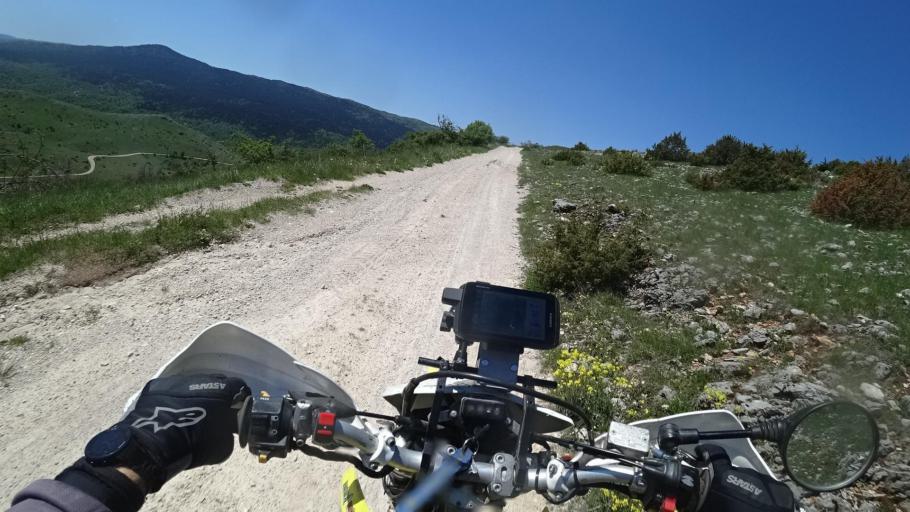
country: BA
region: Federation of Bosnia and Herzegovina
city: Rumboci
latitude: 43.8317
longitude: 17.4362
